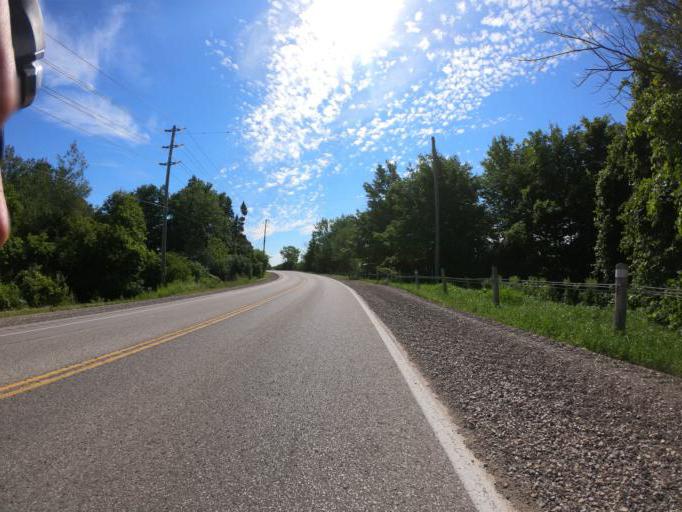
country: CA
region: Ontario
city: Waterloo
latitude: 43.4914
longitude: -80.4480
